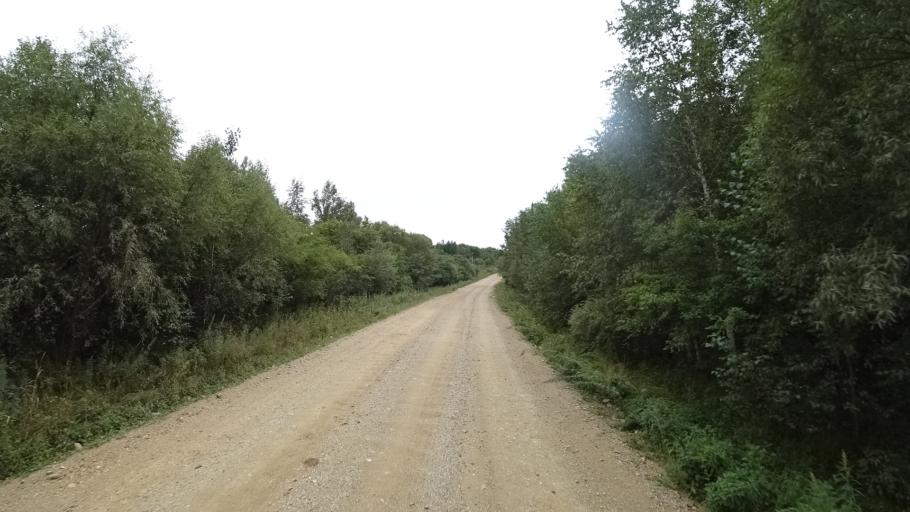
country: RU
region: Primorskiy
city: Lyalichi
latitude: 44.0657
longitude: 132.4782
